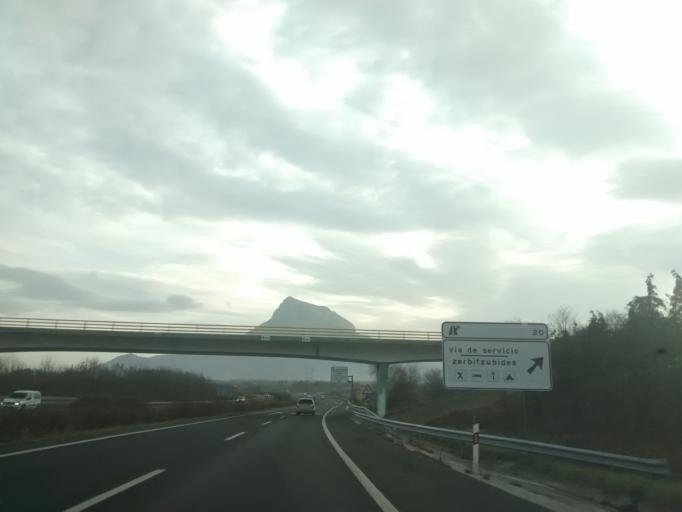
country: ES
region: Navarre
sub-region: Provincia de Navarra
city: Echarri-Aranaz
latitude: 42.8996
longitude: -2.0665
